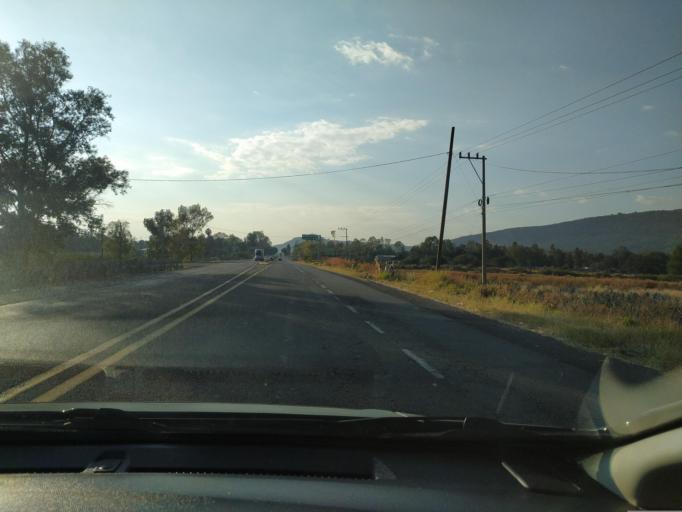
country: MX
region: Jalisco
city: Jamay
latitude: 20.2941
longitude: -102.6702
